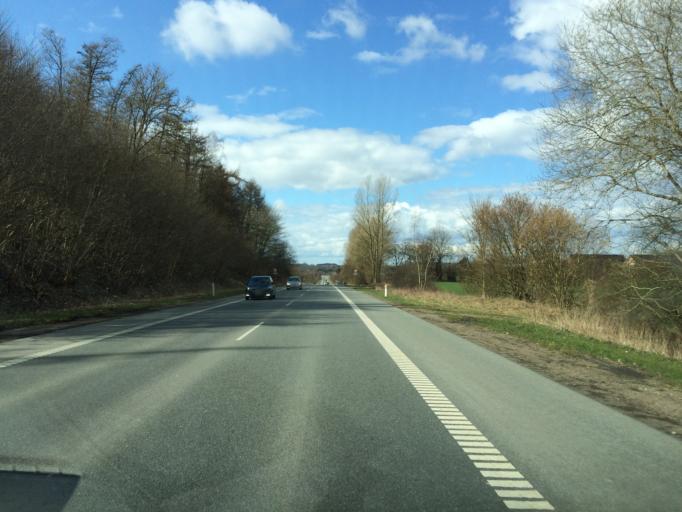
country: DK
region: South Denmark
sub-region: Assens Kommune
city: Vissenbjerg
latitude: 55.3948
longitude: 10.1060
